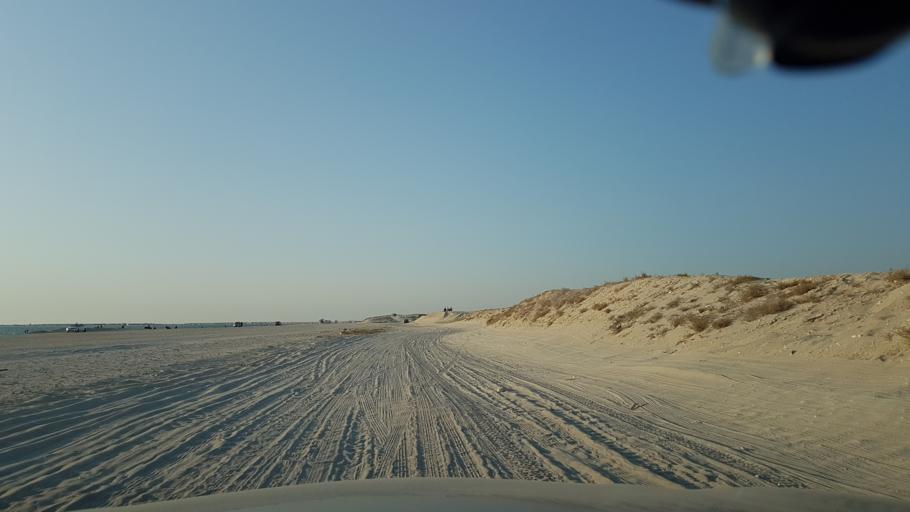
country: BH
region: Manama
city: Jidd Hafs
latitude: 26.2427
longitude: 50.5031
